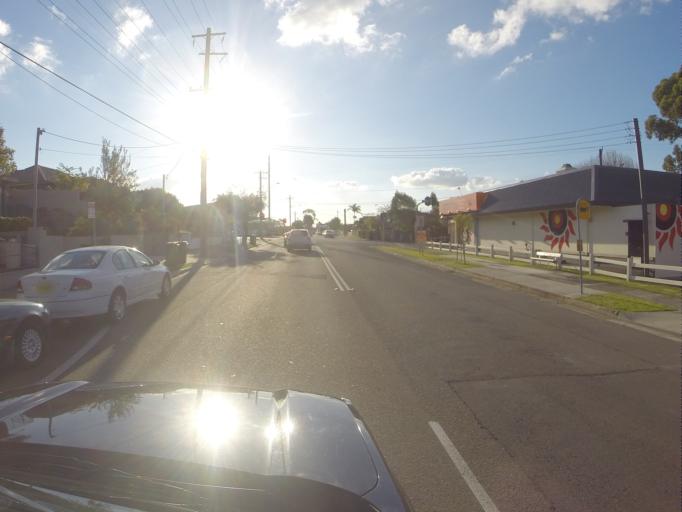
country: AU
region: New South Wales
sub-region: Rockdale
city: Bexley
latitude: -33.9498
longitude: 151.1150
